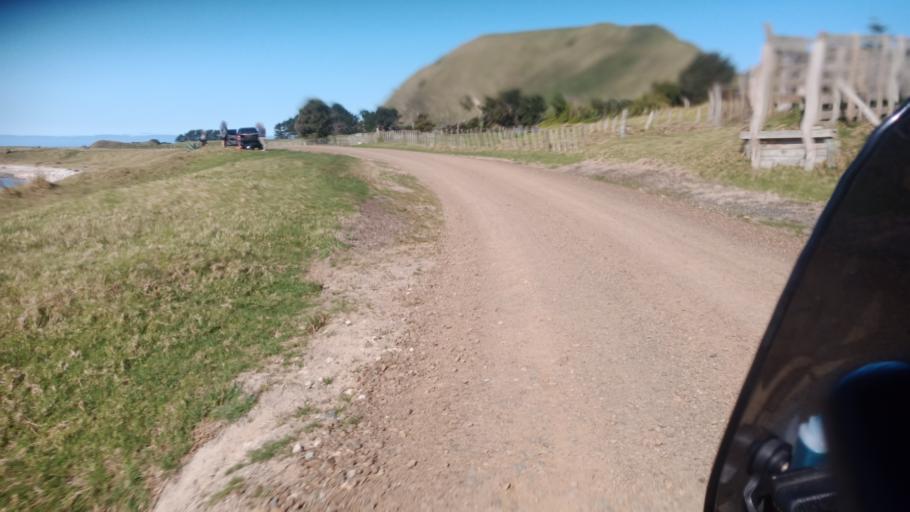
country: NZ
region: Gisborne
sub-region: Gisborne District
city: Gisborne
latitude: -39.0988
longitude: 177.9677
